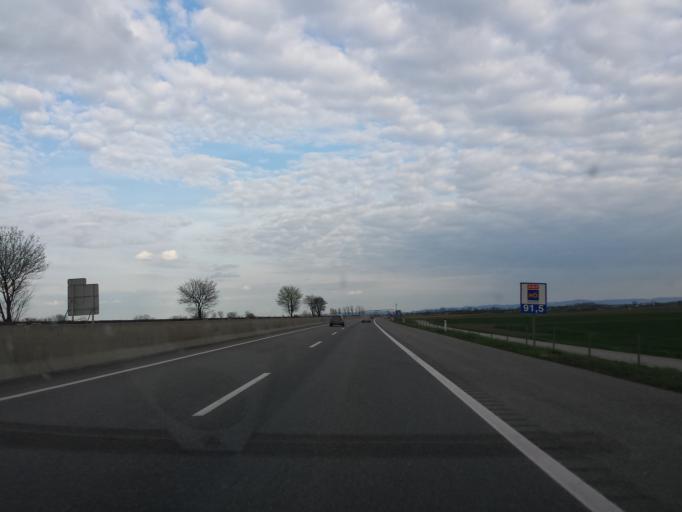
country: AT
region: Lower Austria
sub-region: Politischer Bezirk Tulln
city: Kirchberg am Wagram
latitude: 48.4046
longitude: 15.8906
